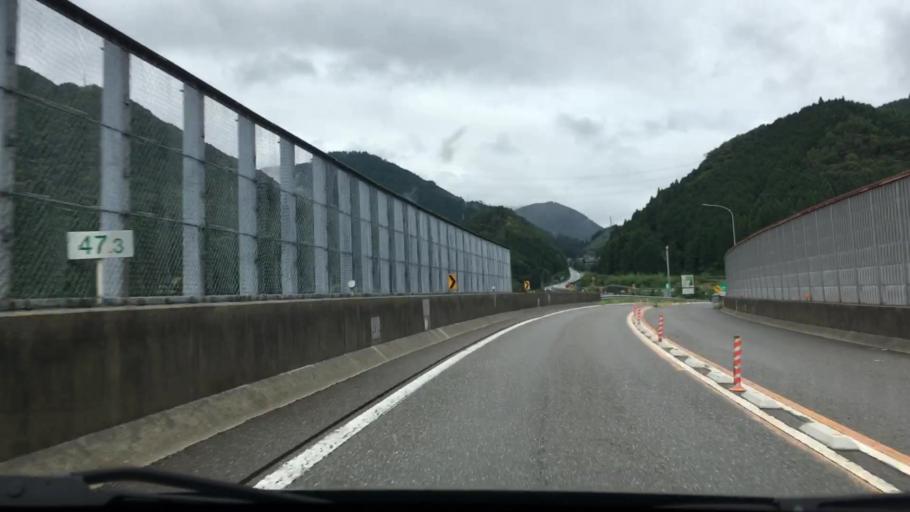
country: JP
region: Hyogo
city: Nishiwaki
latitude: 35.1927
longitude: 134.7909
